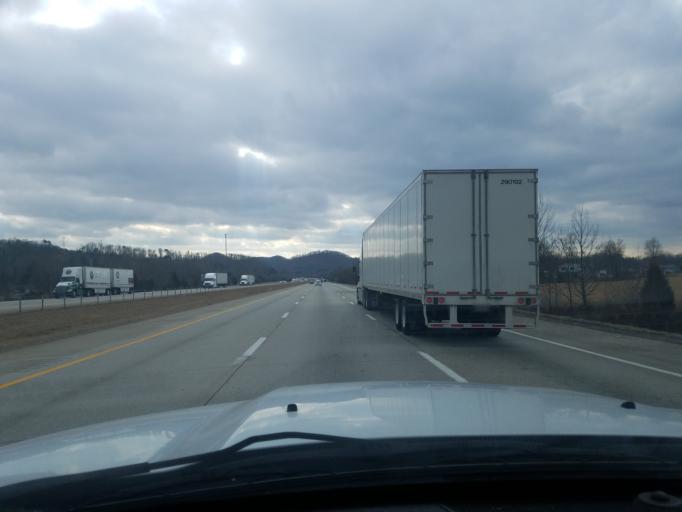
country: US
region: Kentucky
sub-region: Bullitt County
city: Lebanon Junction
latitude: 37.9068
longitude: -85.6920
